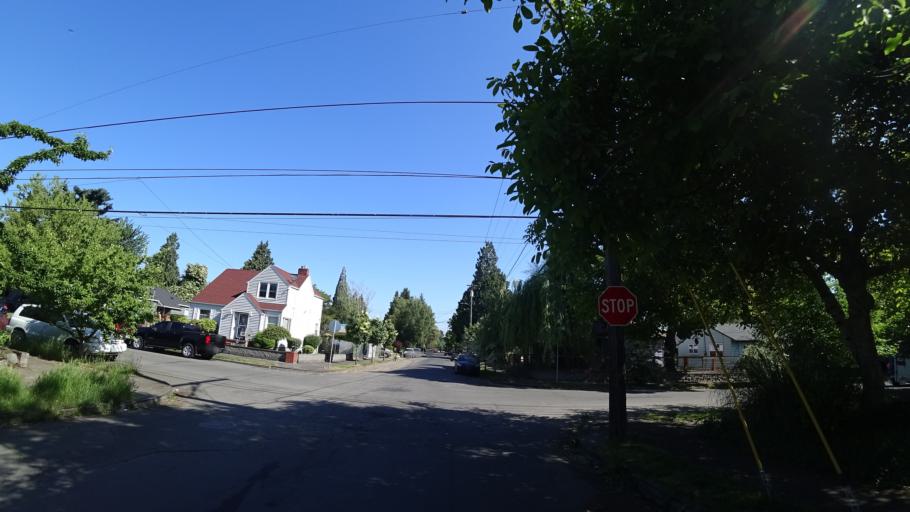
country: US
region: Oregon
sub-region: Multnomah County
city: Portland
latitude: 45.5763
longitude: -122.6634
